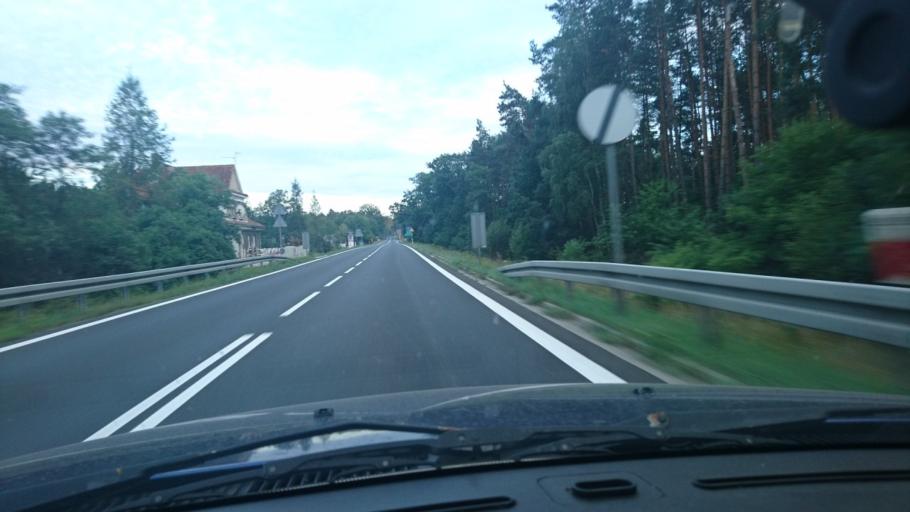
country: PL
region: Silesian Voivodeship
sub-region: Powiat tarnogorski
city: Tworog
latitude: 50.5889
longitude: 18.7024
